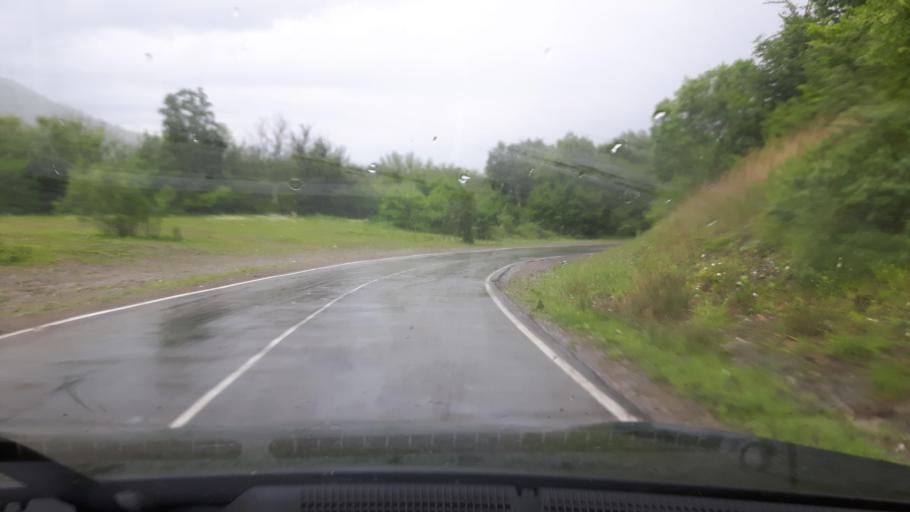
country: GE
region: Kakheti
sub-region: Telavi
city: Telavi
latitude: 41.8926
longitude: 45.3654
